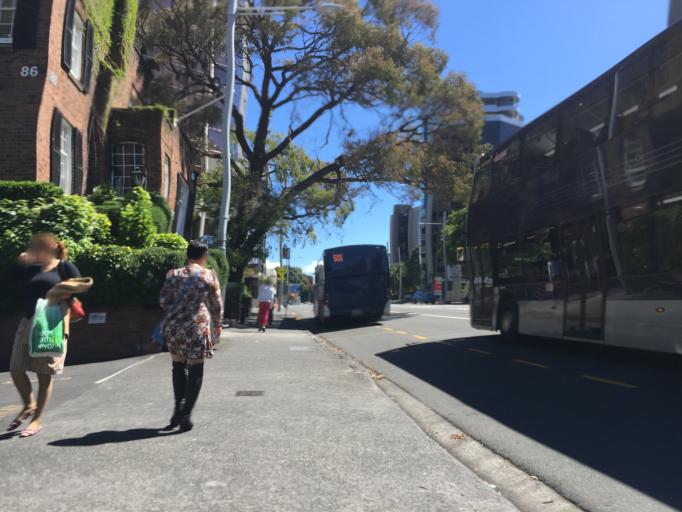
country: NZ
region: Auckland
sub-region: Auckland
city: Auckland
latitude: -36.8566
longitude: 174.7657
